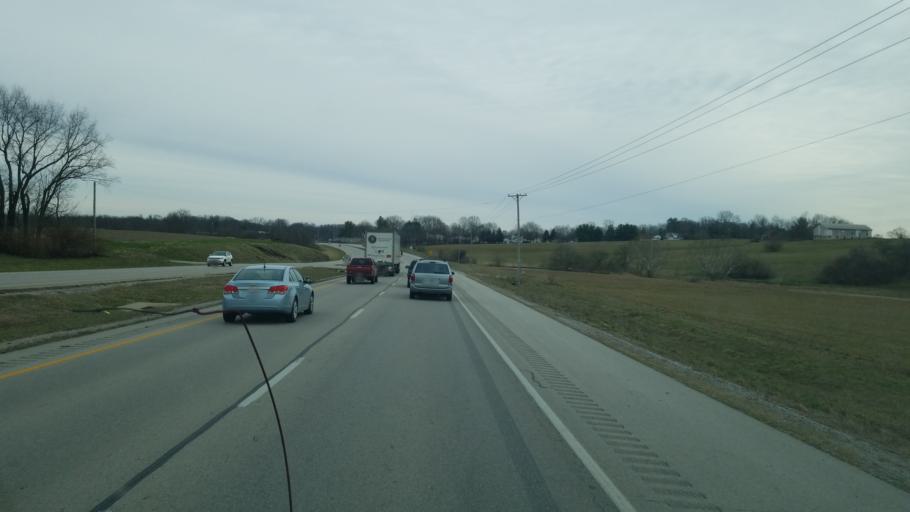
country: US
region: Kentucky
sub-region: Bourbon County
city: Paris
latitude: 38.2254
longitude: -84.2633
